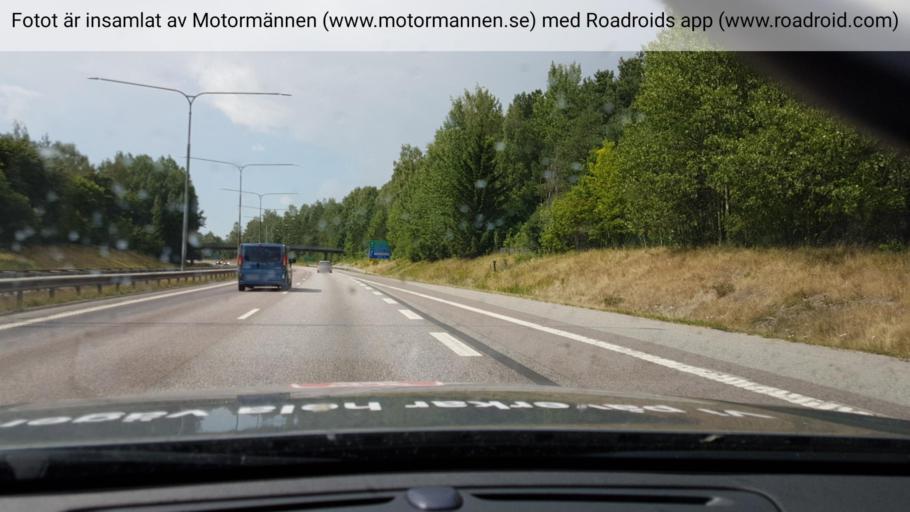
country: SE
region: OErebro
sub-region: Orebro Kommun
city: Orebro
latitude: 59.2930
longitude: 15.1943
